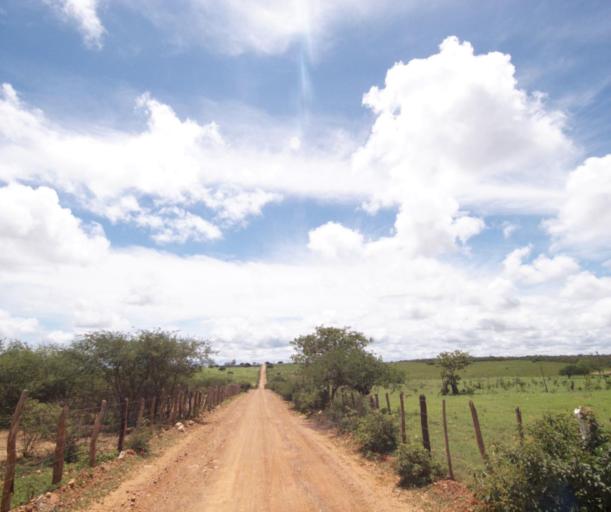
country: BR
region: Bahia
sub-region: Tanhacu
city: Tanhacu
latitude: -14.1901
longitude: -41.0718
